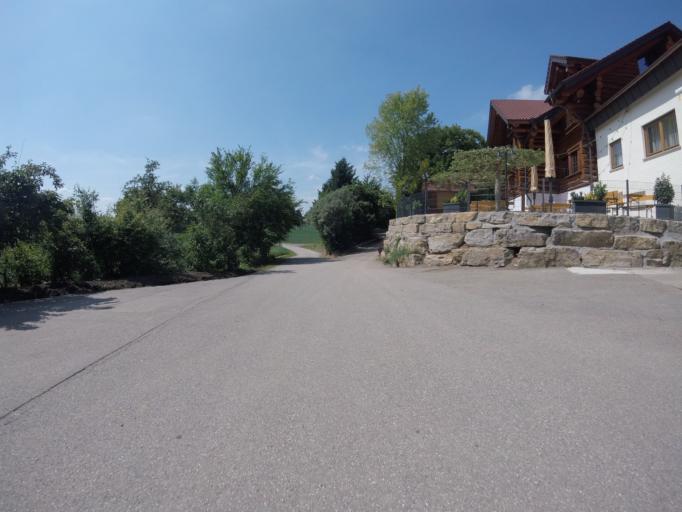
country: DE
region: Baden-Wuerttemberg
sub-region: Regierungsbezirk Stuttgart
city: Abstatt
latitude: 49.0755
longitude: 9.2995
